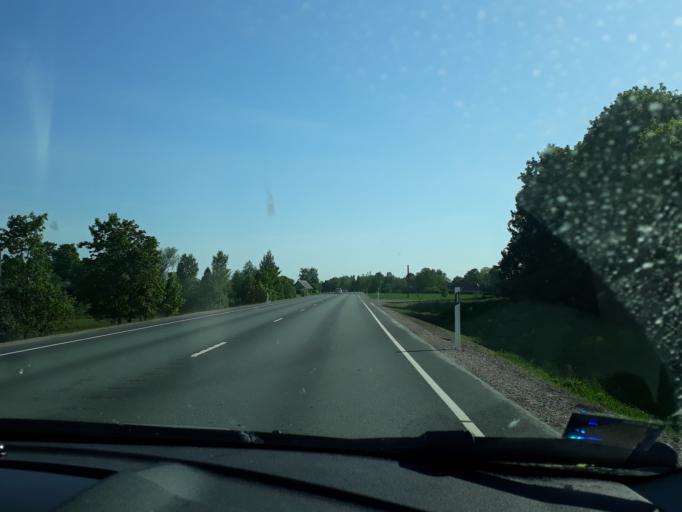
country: EE
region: Paernumaa
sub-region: Tootsi vald
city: Tootsi
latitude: 58.5402
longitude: 24.8398
